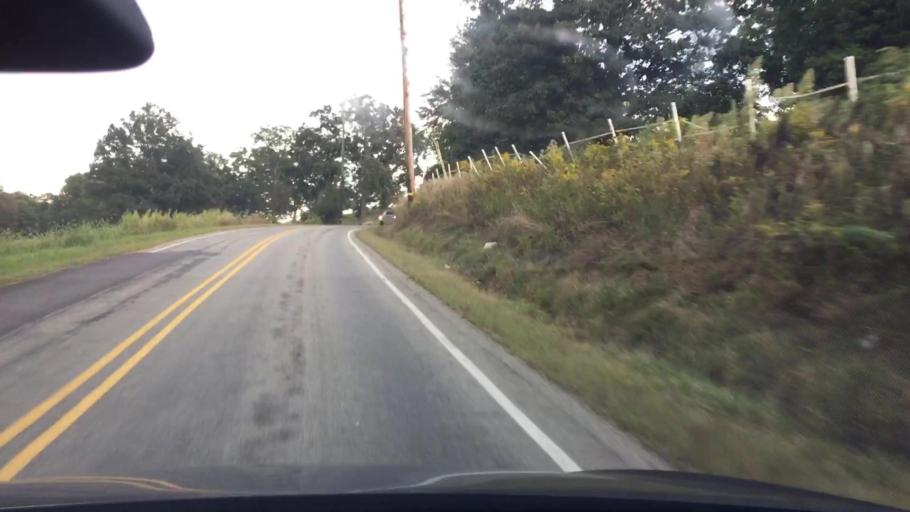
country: US
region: Pennsylvania
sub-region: Butler County
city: Meadowood
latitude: 40.8384
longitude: -79.8783
